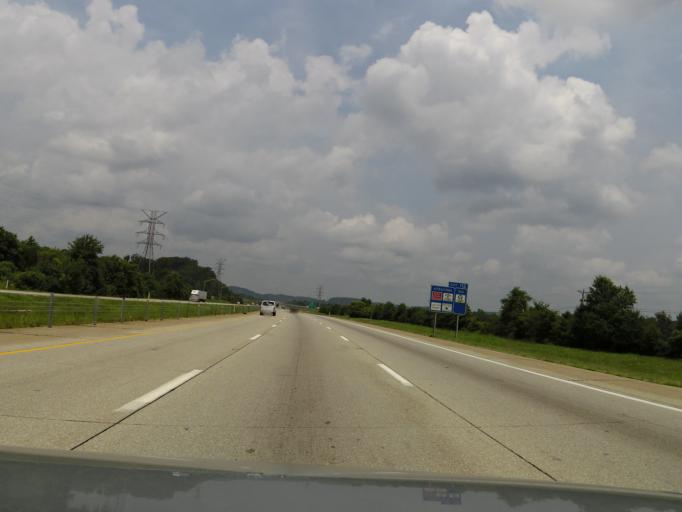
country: US
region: Kentucky
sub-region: Bullitt County
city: Shepherdsville
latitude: 37.9160
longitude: -85.6870
